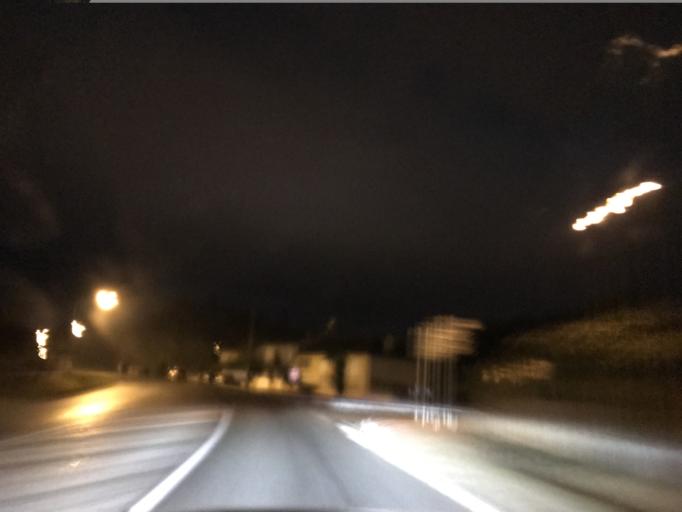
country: FR
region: Auvergne
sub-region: Departement de l'Allier
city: Hauterive
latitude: 46.0906
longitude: 3.4424
